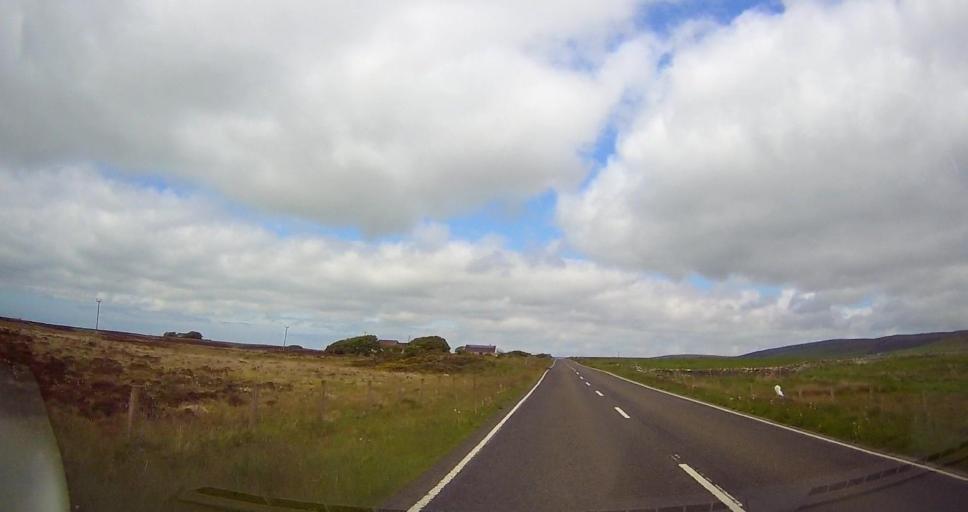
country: GB
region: Scotland
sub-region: Orkney Islands
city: Stromness
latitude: 59.0067
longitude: -3.1550
